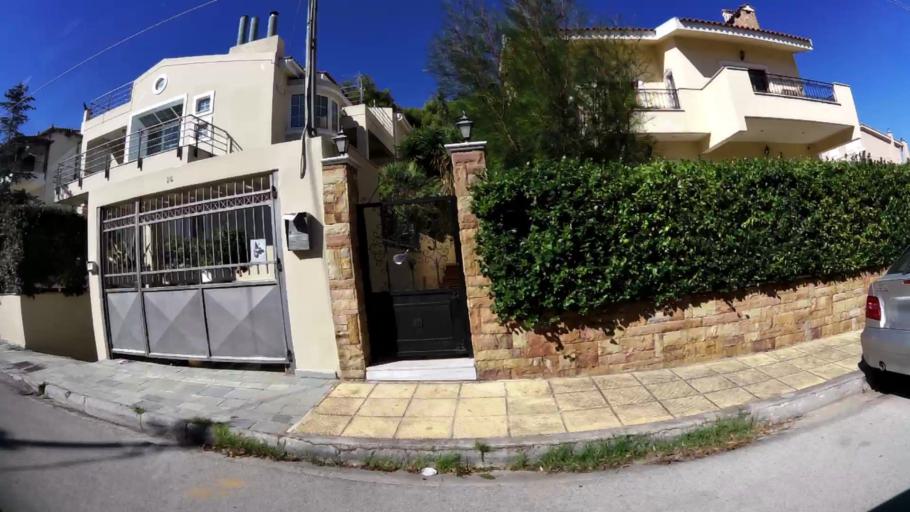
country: GR
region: Attica
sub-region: Nomarchia Athinas
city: Kifisia
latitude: 38.0887
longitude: 23.7930
